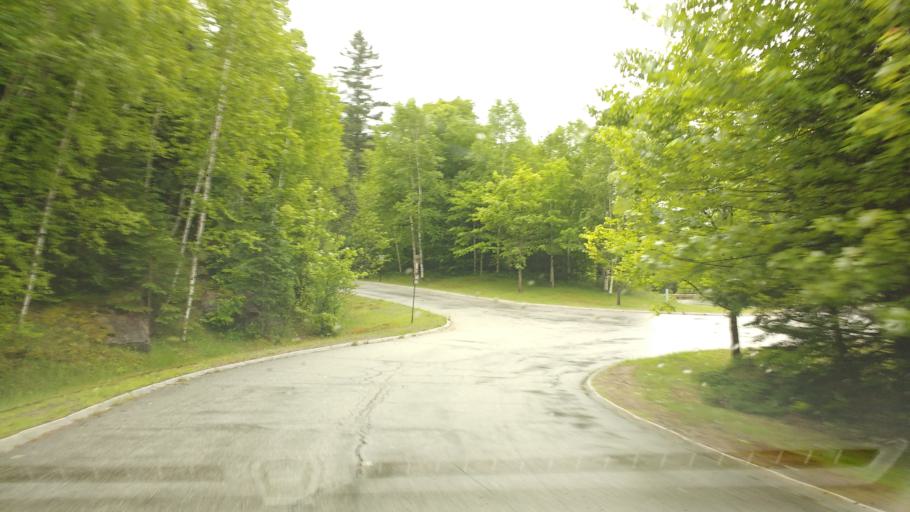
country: US
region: New Hampshire
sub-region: Grafton County
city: Woodstock
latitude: 44.1003
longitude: -71.6822
